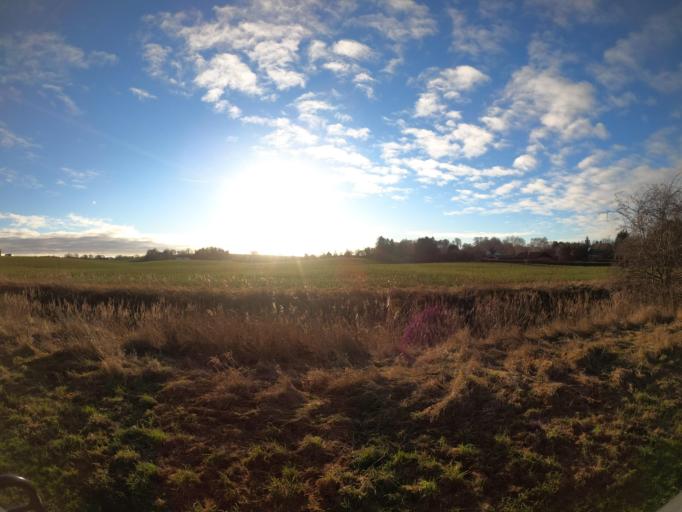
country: SE
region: Skane
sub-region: Svedala Kommun
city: Svedala
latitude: 55.5050
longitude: 13.2291
